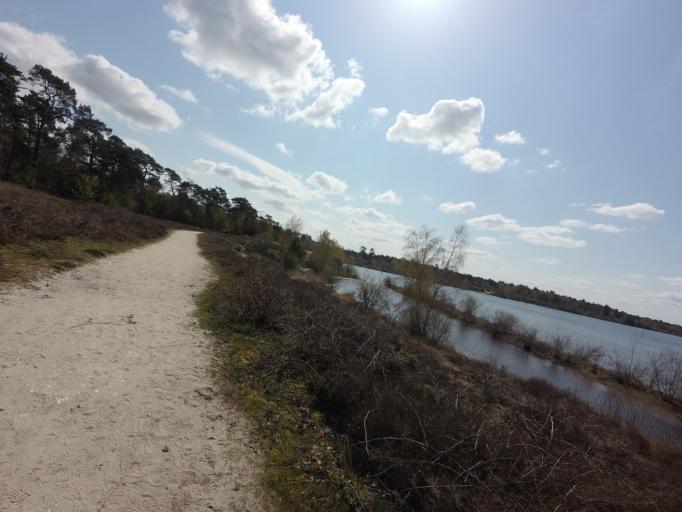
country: NL
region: Limburg
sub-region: Gemeente Bergen
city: Wellerlooi
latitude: 51.5758
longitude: 6.1066
